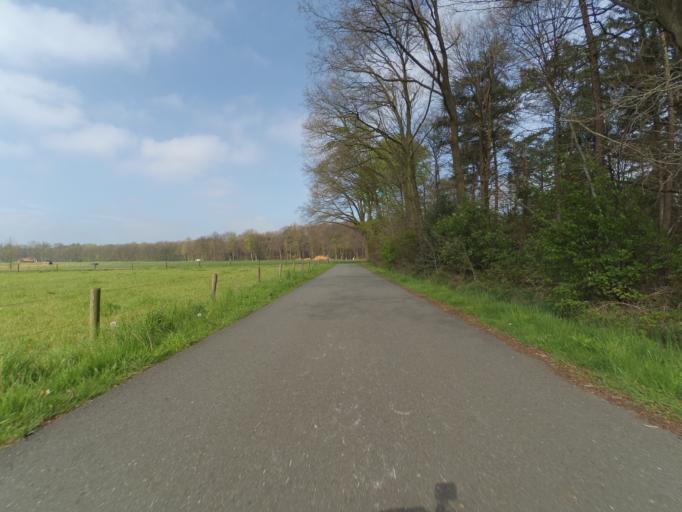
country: NL
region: Gelderland
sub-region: Gemeente Apeldoorn
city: Uddel
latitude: 52.2781
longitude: 5.7600
